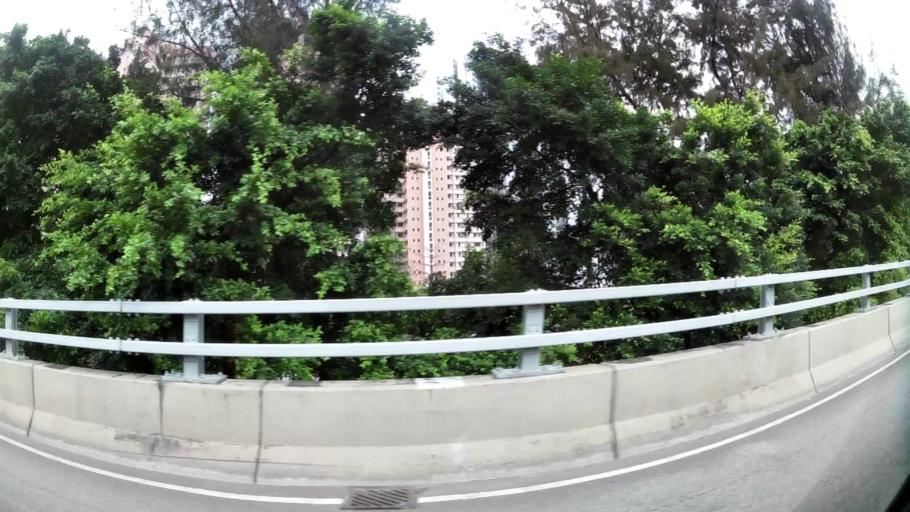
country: HK
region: Tuen Mun
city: Tuen Mun
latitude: 22.4057
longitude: 113.9753
